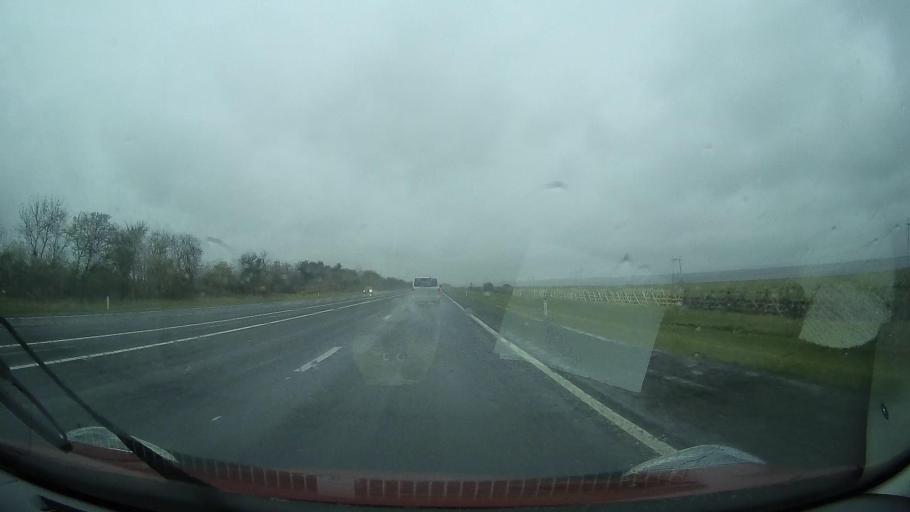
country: RU
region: Stavropol'skiy
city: Nevinnomyssk
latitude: 44.6121
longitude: 42.1185
